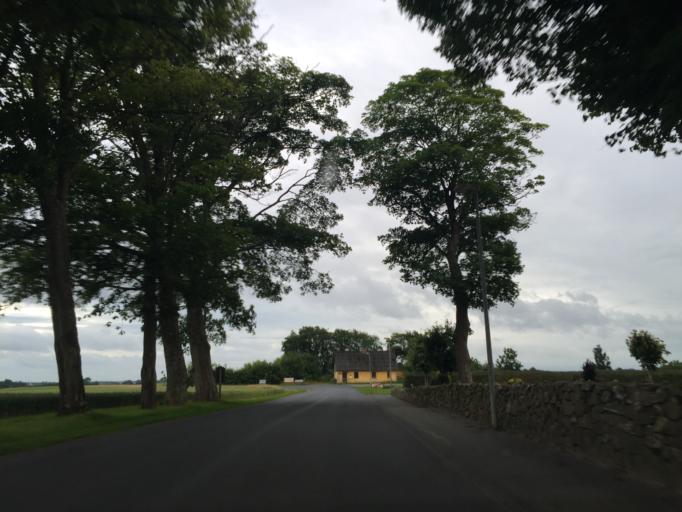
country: DK
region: Central Jutland
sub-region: Silkeborg Kommune
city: Silkeborg
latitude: 56.2363
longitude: 9.5467
